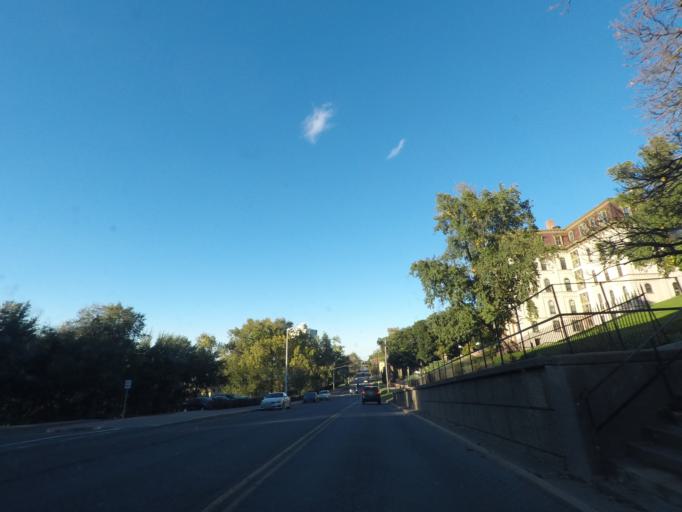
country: US
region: New York
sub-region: Rensselaer County
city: Troy
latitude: 42.7311
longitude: -73.6840
